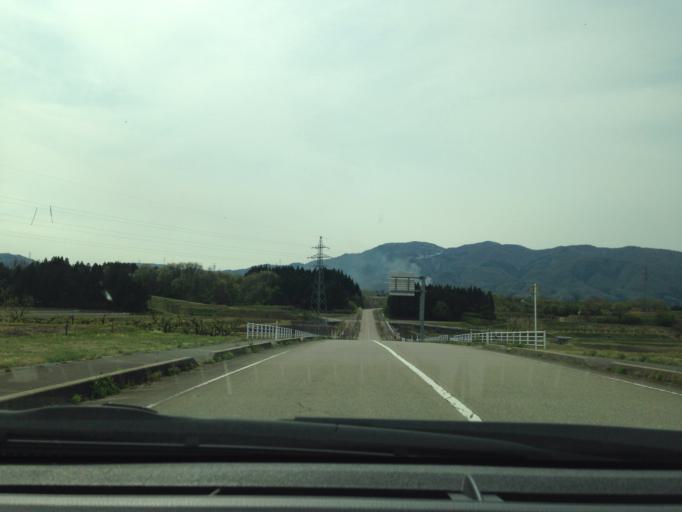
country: JP
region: Toyama
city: Fukumitsu
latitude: 36.5195
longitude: 136.8821
